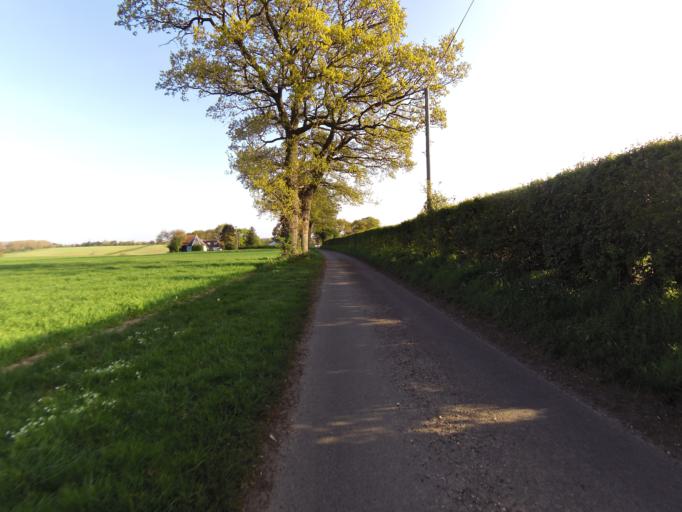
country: GB
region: England
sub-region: Suffolk
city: Capel Saint Mary
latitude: 52.0380
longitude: 1.0724
